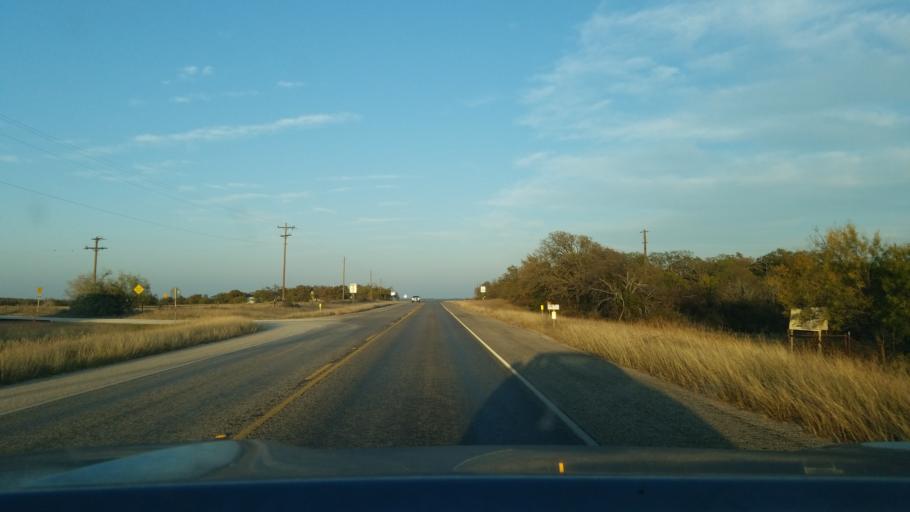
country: US
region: Texas
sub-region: Eastland County
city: Cisco
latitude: 32.3986
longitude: -98.9664
